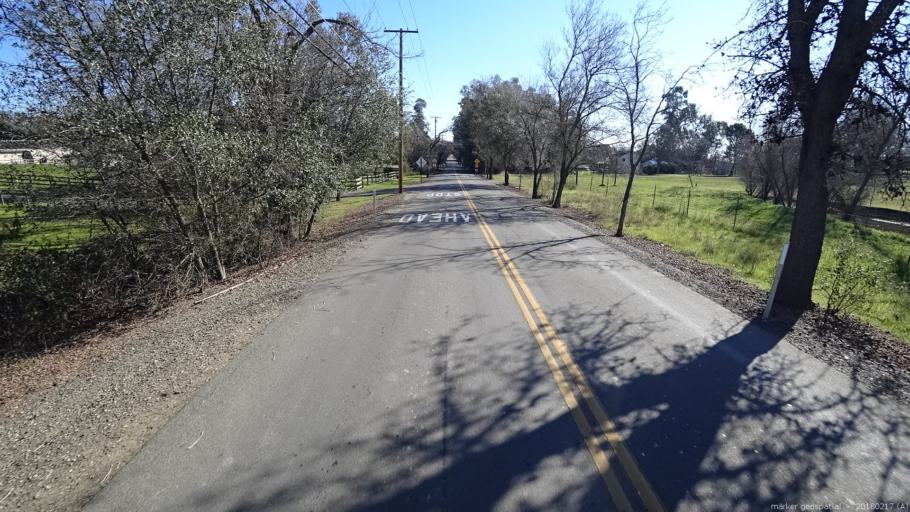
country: US
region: California
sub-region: Sacramento County
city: Orangevale
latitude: 38.7110
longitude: -121.2148
